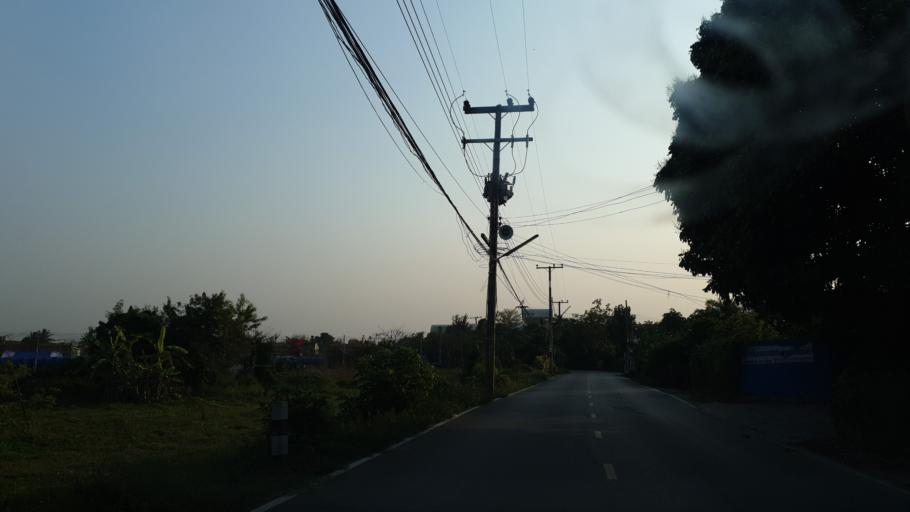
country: TH
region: Chiang Mai
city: Saraphi
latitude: 18.7100
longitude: 99.0273
